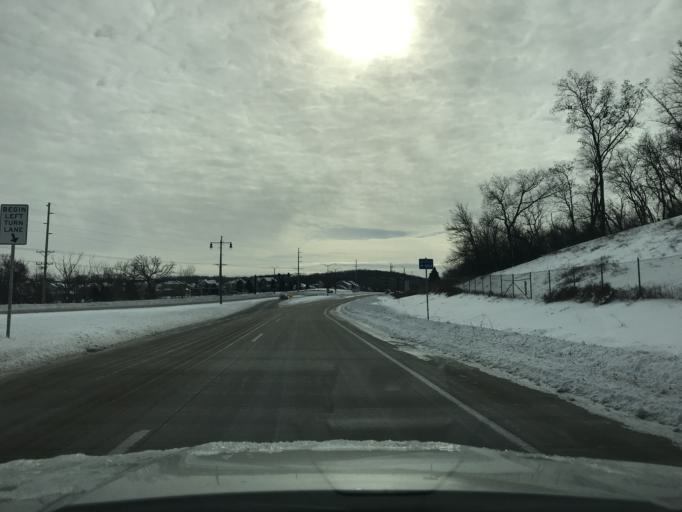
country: US
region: Wisconsin
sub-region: Dane County
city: Sun Prairie
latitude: 43.1587
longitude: -89.2661
